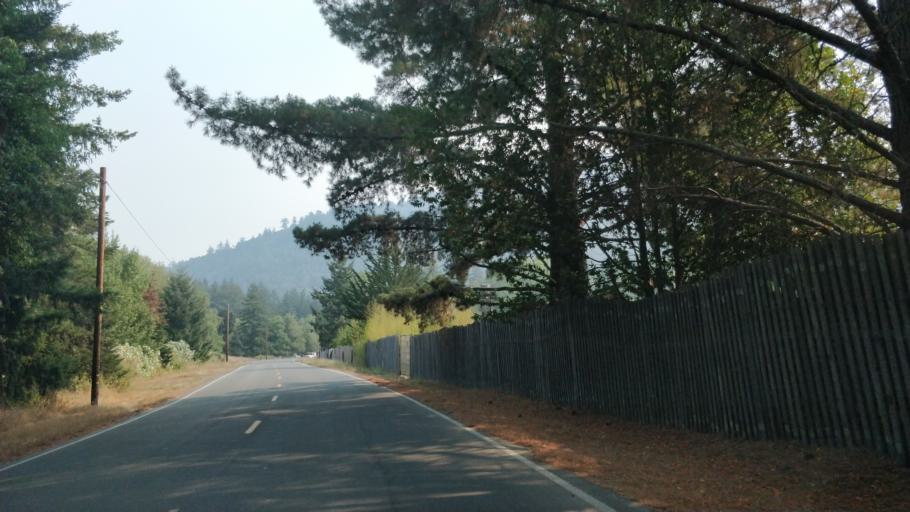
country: US
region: California
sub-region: Humboldt County
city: Rio Dell
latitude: 40.3186
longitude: -124.2852
